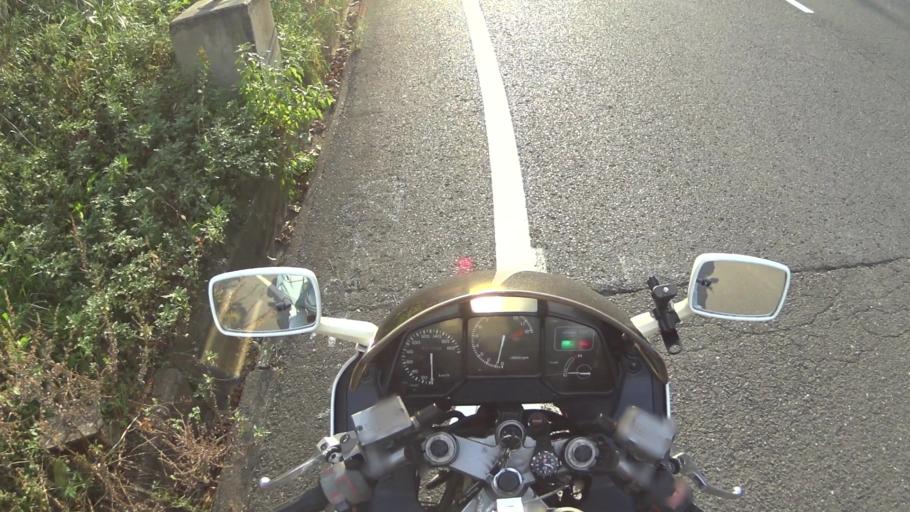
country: JP
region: Kyoto
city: Maizuru
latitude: 35.5163
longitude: 135.4578
